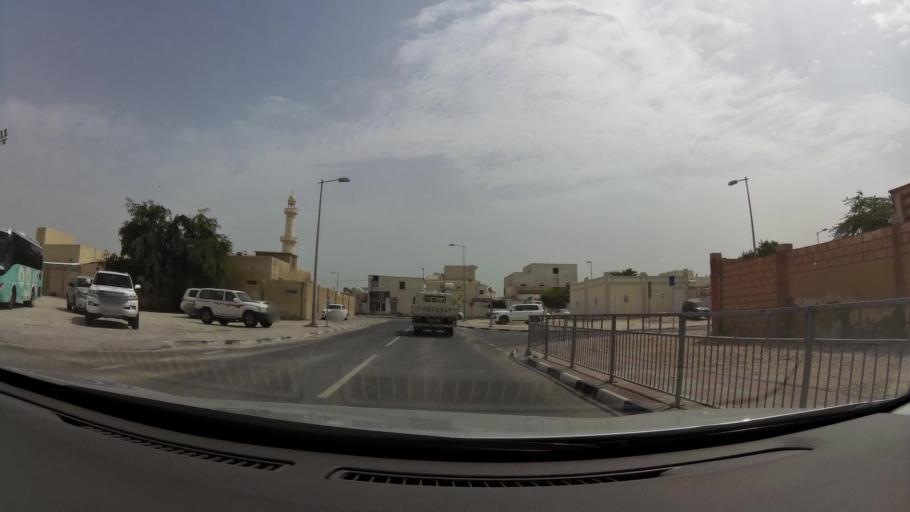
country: QA
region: Baladiyat ad Dawhah
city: Doha
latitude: 25.3125
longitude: 51.4806
